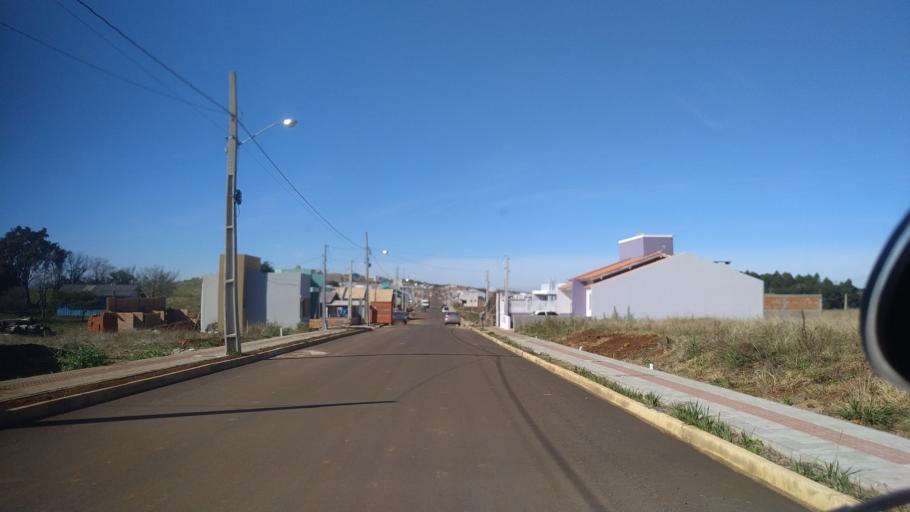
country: BR
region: Santa Catarina
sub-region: Chapeco
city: Chapeco
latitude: -27.0486
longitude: -52.6001
